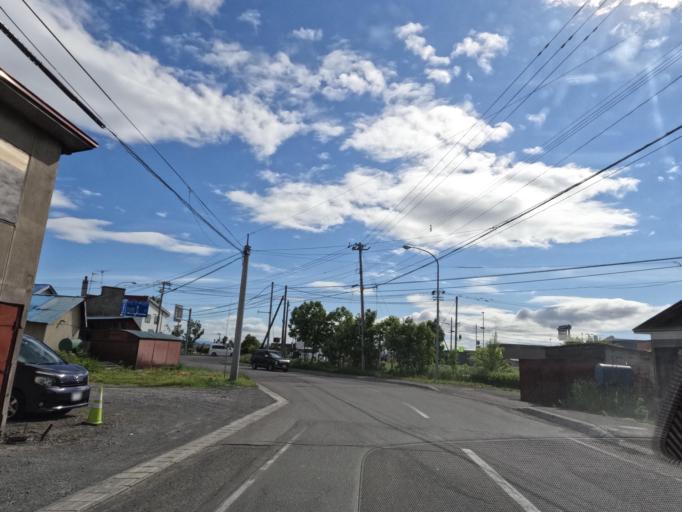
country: JP
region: Hokkaido
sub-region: Asahikawa-shi
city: Asahikawa
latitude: 43.8229
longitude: 142.5171
